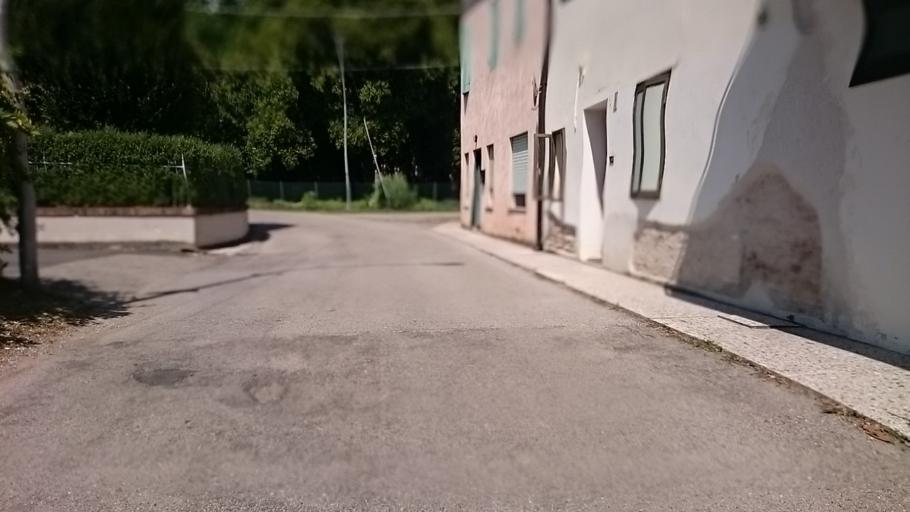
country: IT
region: Veneto
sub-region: Provincia di Vicenza
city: Rosa
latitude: 45.7264
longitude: 11.7349
